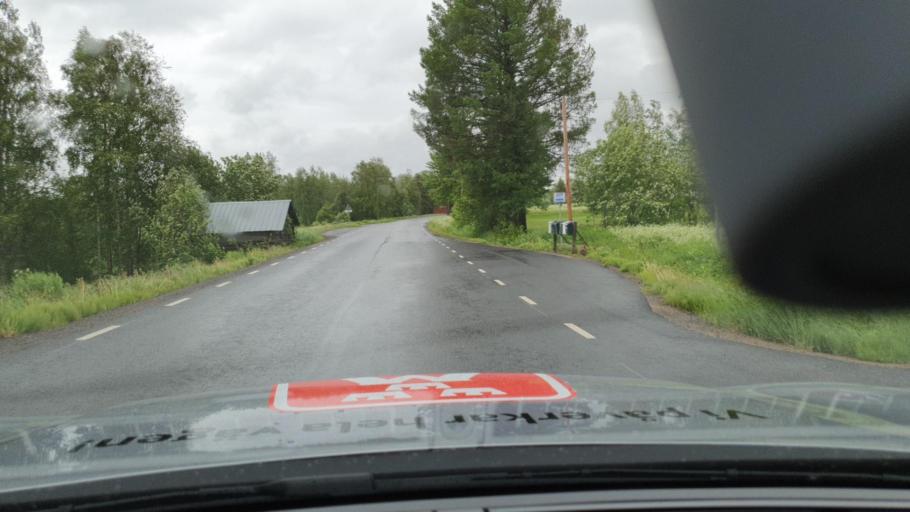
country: FI
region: Lapland
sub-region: Torniolaakso
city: Ylitornio
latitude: 66.1992
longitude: 23.7104
